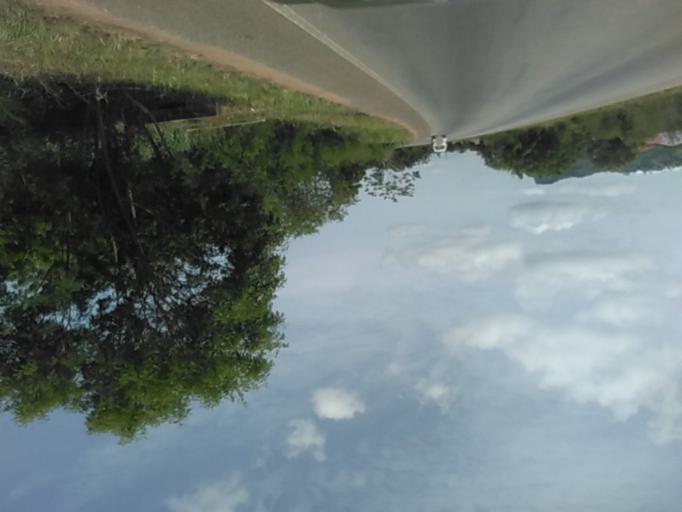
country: GH
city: Akropong
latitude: 6.1125
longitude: 0.0498
